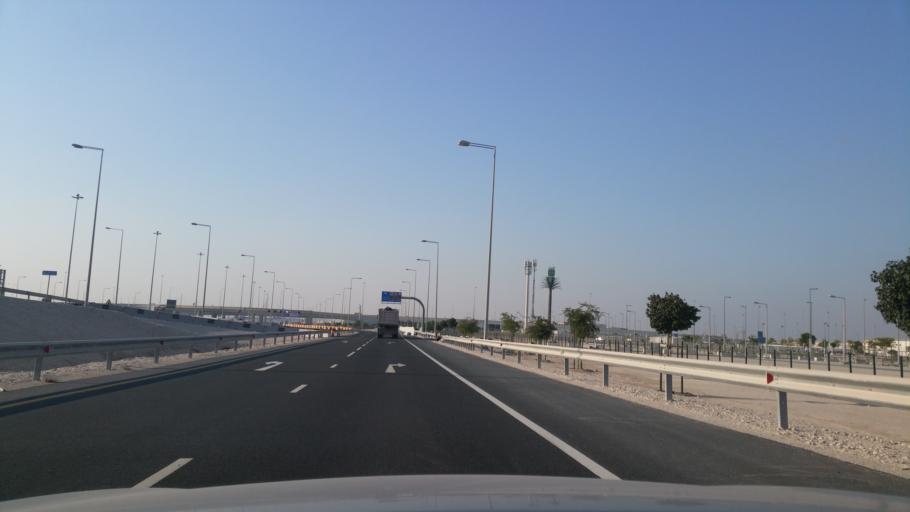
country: QA
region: Al Wakrah
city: Al Wakrah
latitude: 25.1578
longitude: 51.5717
